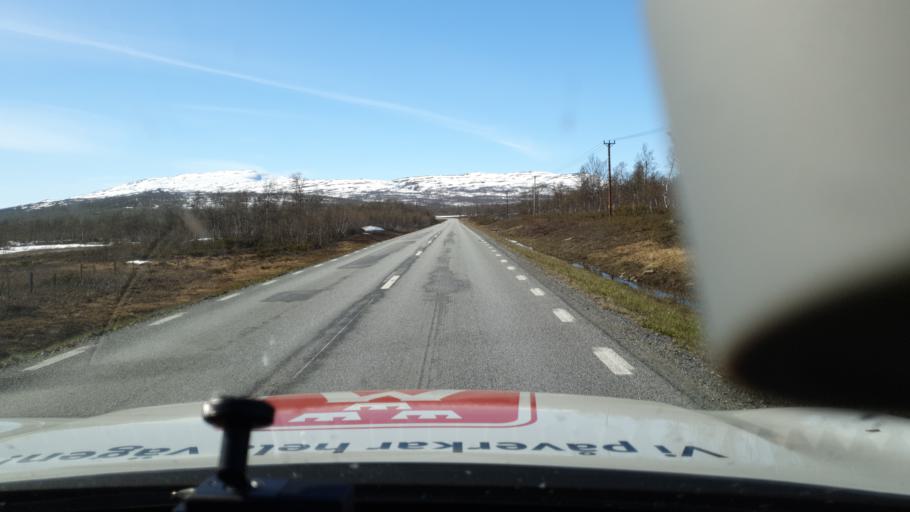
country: NO
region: Nordland
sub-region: Rana
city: Mo i Rana
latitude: 66.0316
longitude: 15.0745
